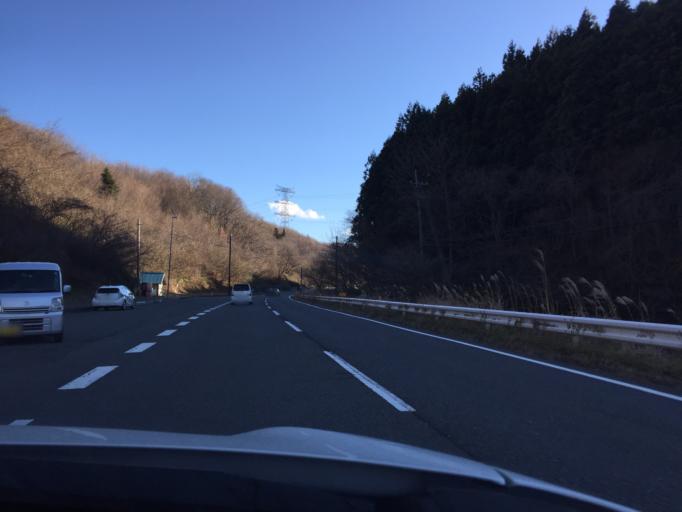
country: JP
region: Fukushima
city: Ishikawa
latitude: 37.1835
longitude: 140.6475
